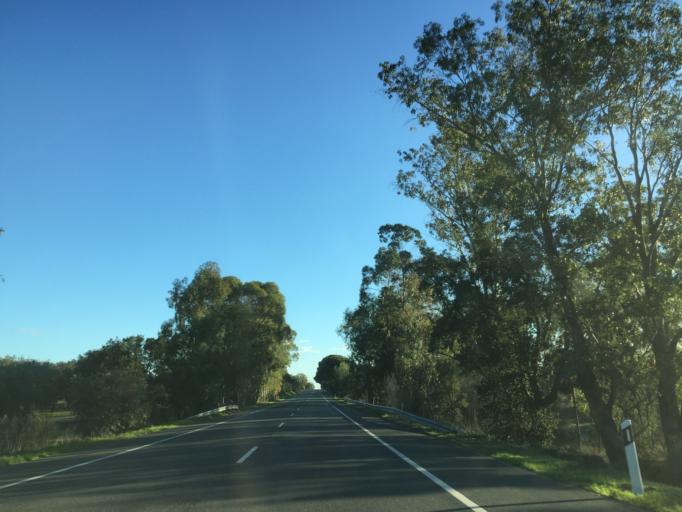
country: PT
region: Setubal
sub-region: Grandola
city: Grandola
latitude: 38.0310
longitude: -8.4002
